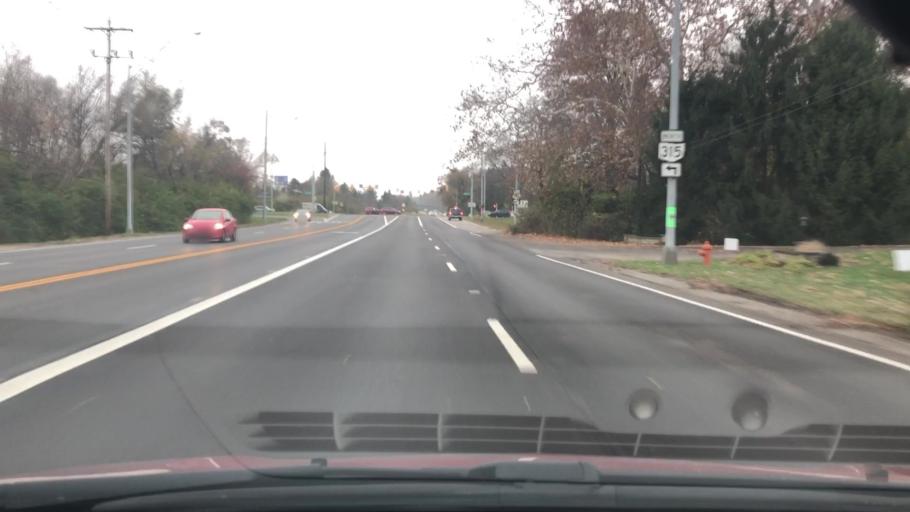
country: US
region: Ohio
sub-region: Franklin County
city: Worthington
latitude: 40.0536
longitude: -83.0338
